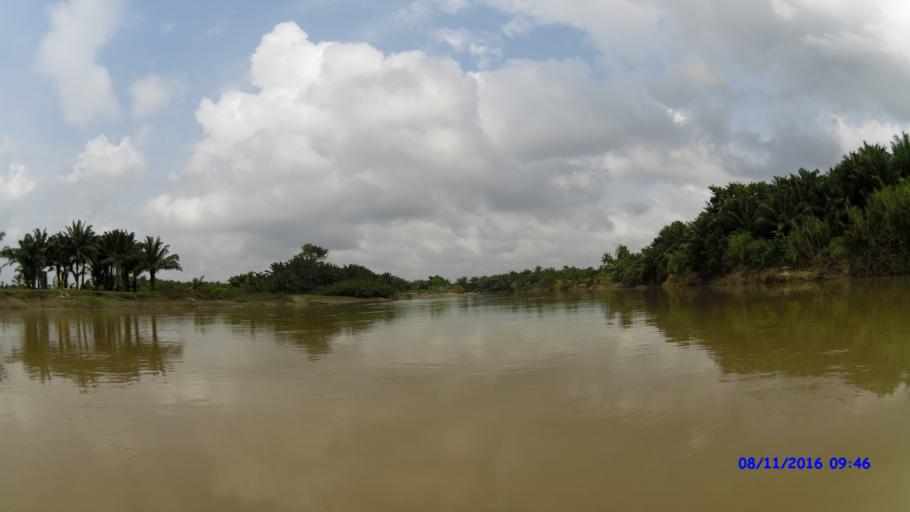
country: BJ
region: Mono
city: Come
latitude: 6.4286
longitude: 1.7740
